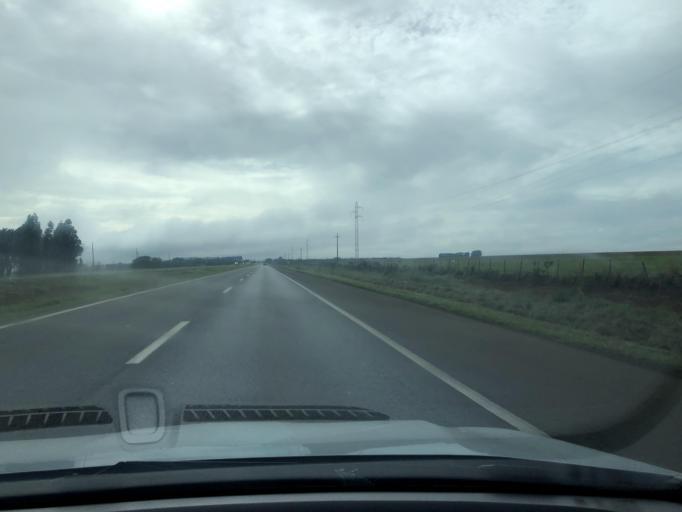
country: BR
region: Goias
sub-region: Cristalina
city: Cristalina
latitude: -16.7078
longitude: -47.6842
